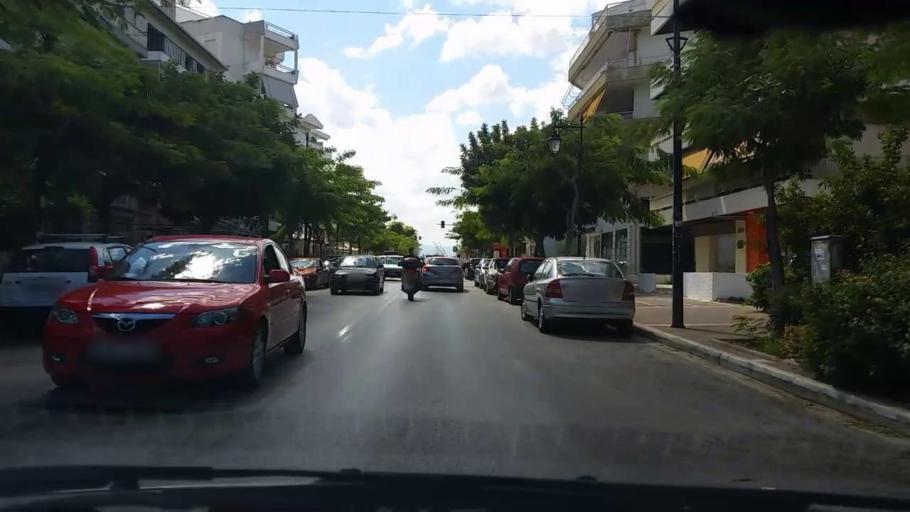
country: GR
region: Peloponnese
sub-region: Nomos Korinthias
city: Loutraki
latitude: 37.9707
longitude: 22.9779
